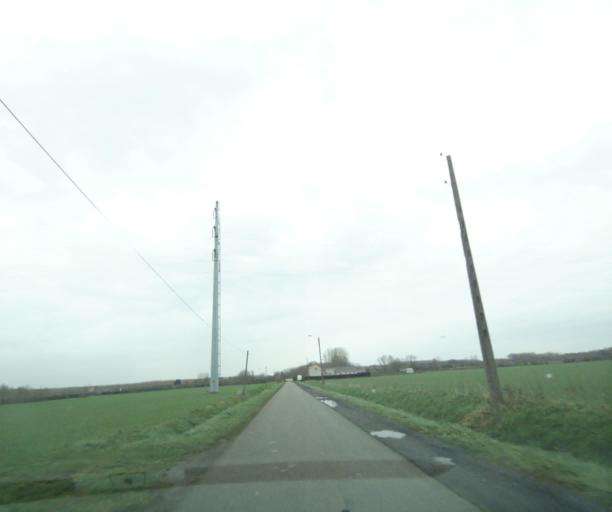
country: FR
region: Nord-Pas-de-Calais
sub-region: Departement du Nord
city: Vicq
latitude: 50.4149
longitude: 3.6139
